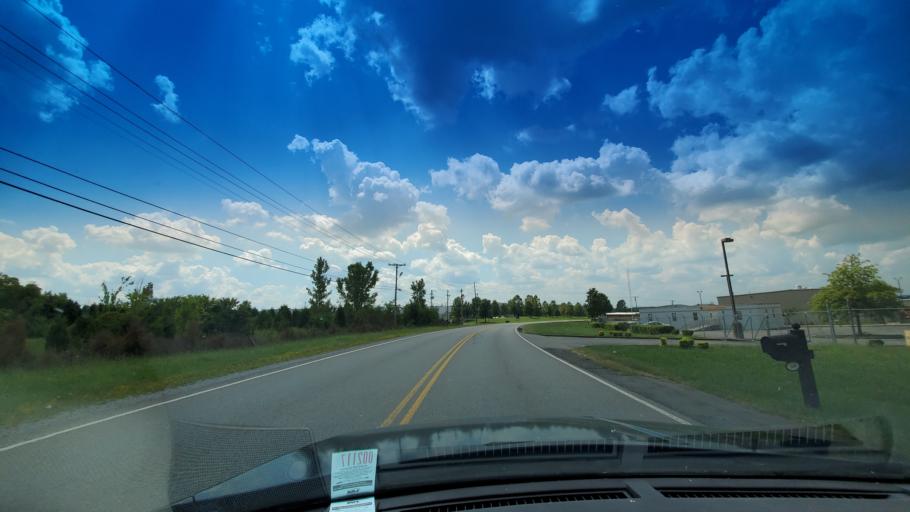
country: US
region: Tennessee
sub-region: Wilson County
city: Lebanon
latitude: 36.1735
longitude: -86.2868
